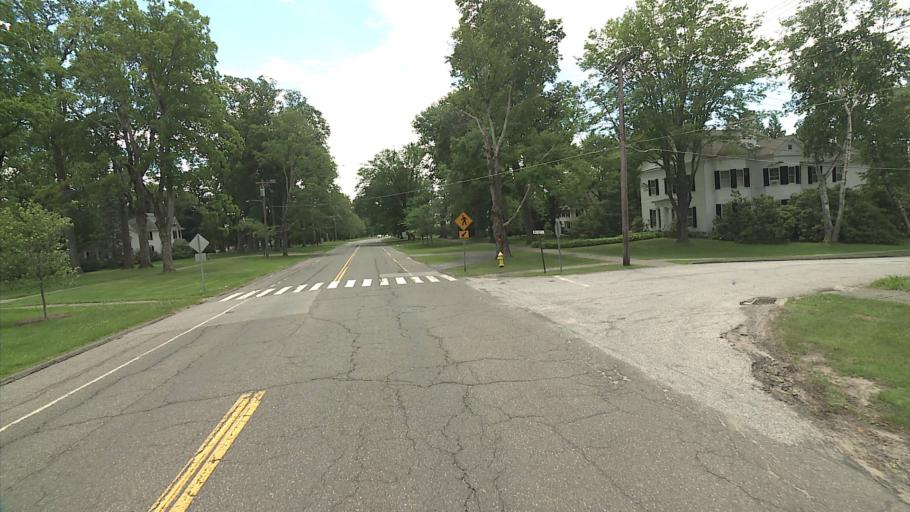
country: US
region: Connecticut
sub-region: Litchfield County
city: Litchfield
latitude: 41.7432
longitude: -73.1879
